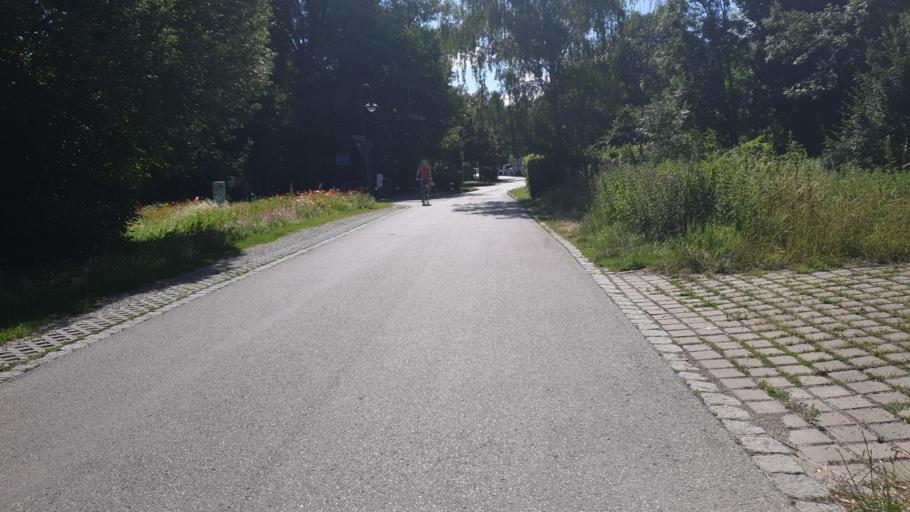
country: DE
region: Bavaria
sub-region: Upper Bavaria
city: Puchheim
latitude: 48.1715
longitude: 11.3564
